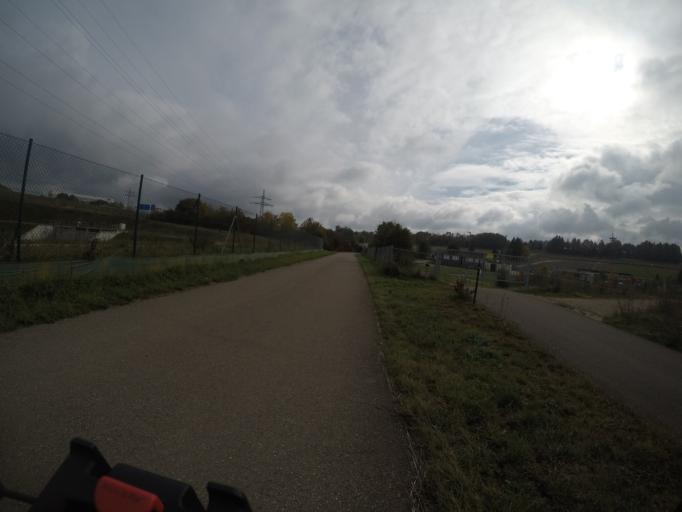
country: DE
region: Baden-Wuerttemberg
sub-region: Tuebingen Region
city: Dornstadt
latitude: 48.4557
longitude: 9.9481
